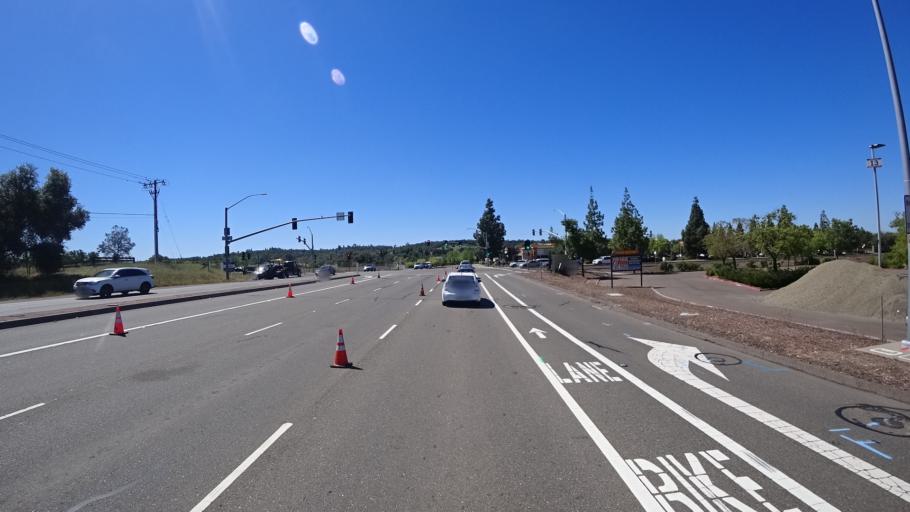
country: US
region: California
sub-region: Placer County
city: Rocklin
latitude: 38.7892
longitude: -121.2061
